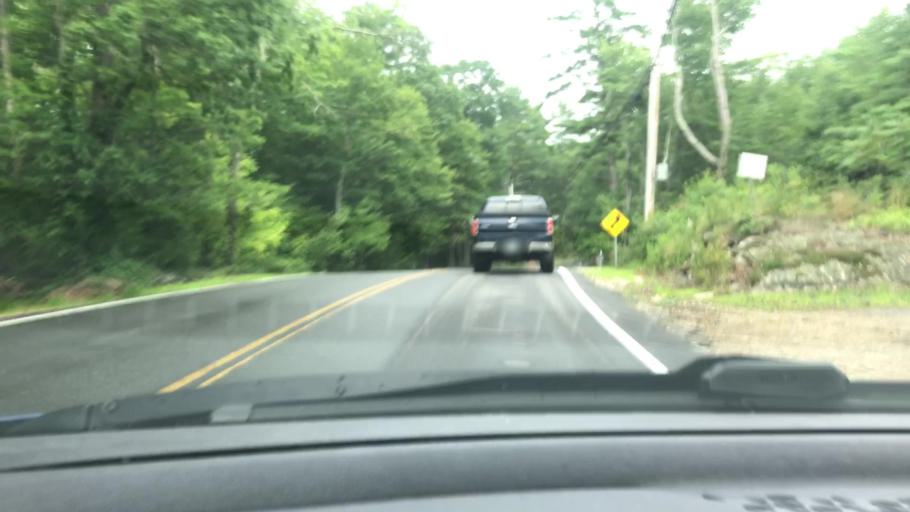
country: US
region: New Hampshire
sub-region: Merrimack County
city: Epsom
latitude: 43.2087
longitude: -71.2794
